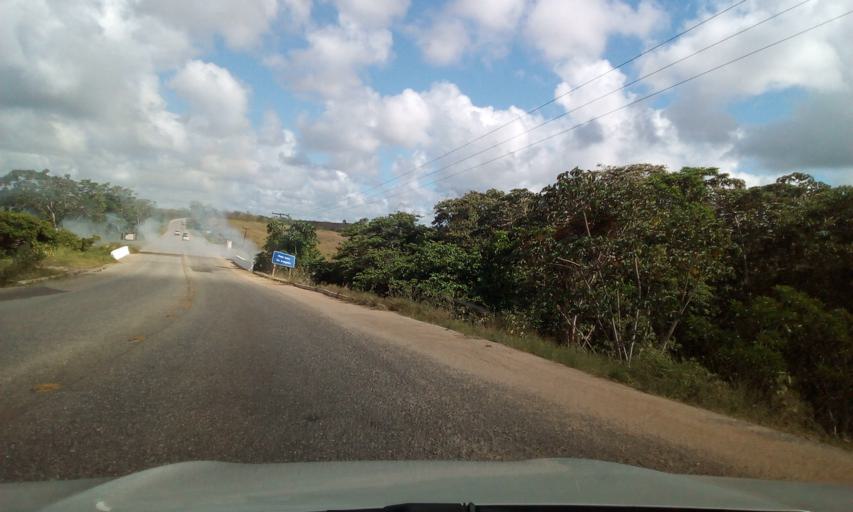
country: BR
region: Sergipe
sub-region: Estancia
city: Estancia
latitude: -11.3500
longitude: -37.4484
